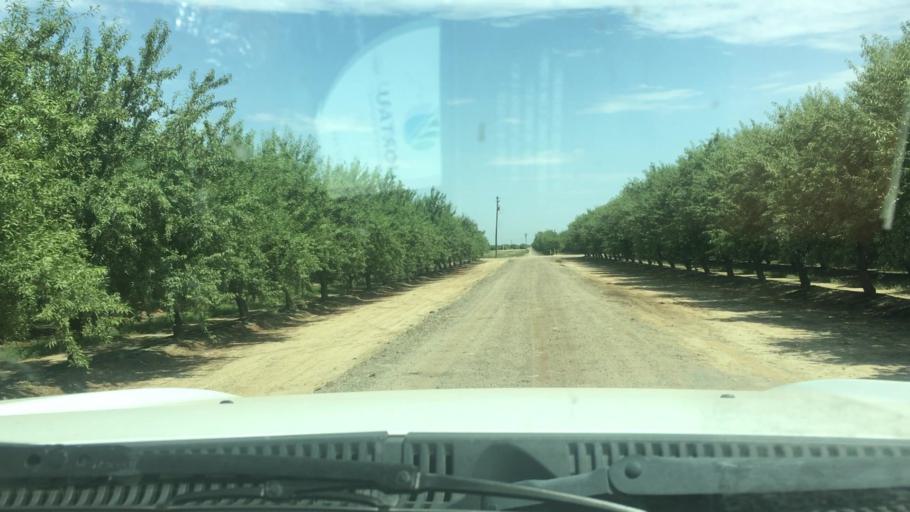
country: US
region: California
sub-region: Kern County
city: Wasco
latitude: 35.5564
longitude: -119.4296
